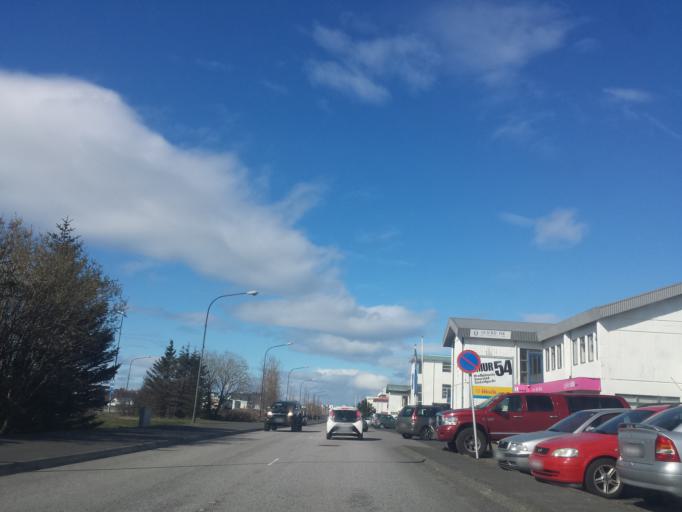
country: IS
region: Capital Region
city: Hafnarfjoerdur
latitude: 64.0774
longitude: -21.9400
